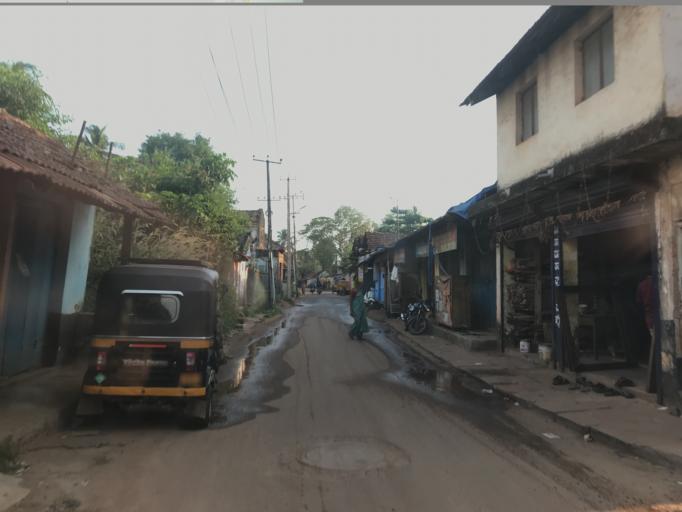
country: IN
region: Karnataka
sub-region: Dakshina Kannada
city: Ullal
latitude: 12.8509
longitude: 74.8372
